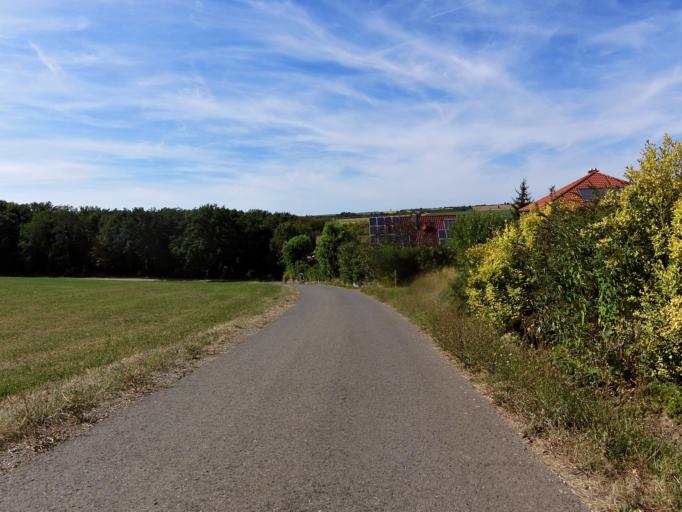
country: DE
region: Bavaria
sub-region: Regierungsbezirk Unterfranken
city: Theilheim
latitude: 49.7499
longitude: 10.0222
